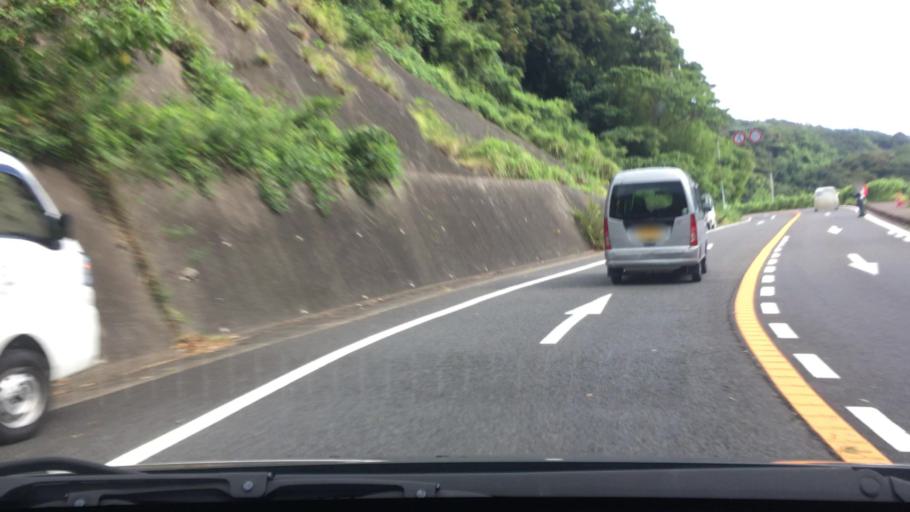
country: JP
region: Nagasaki
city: Togitsu
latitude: 32.8421
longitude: 129.7060
